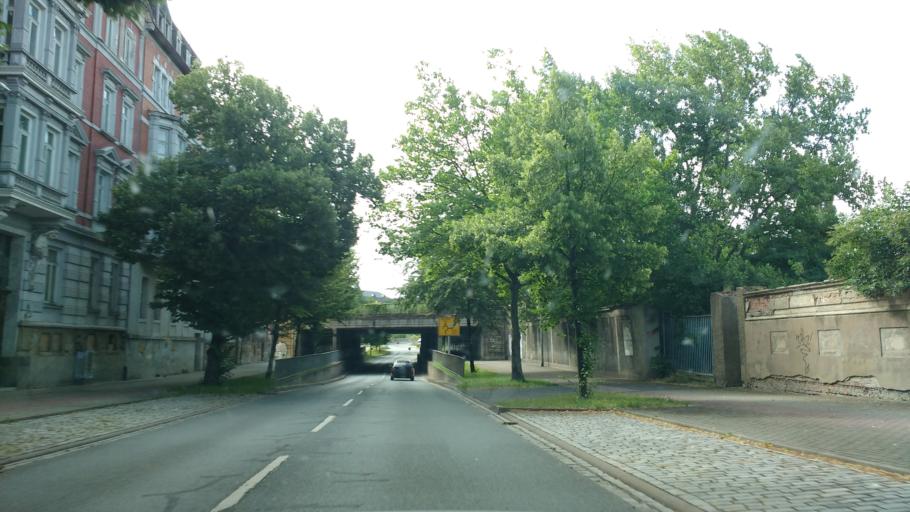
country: DE
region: Saxony-Anhalt
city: Zeitz
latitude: 51.0573
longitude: 12.1350
